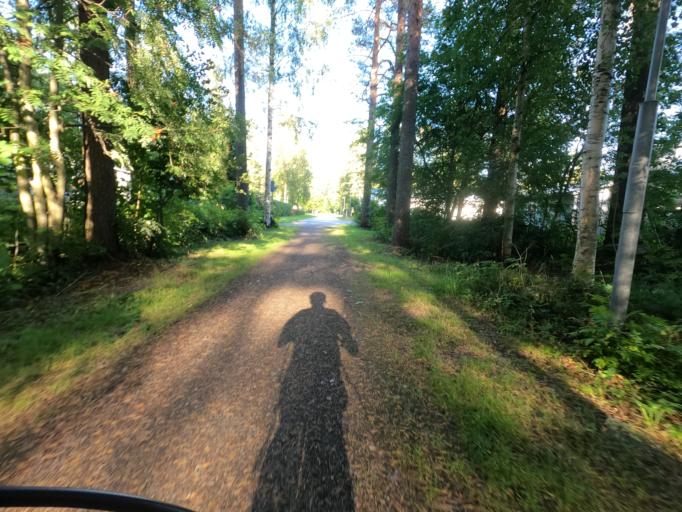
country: FI
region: North Karelia
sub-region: Joensuu
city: Joensuu
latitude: 62.6140
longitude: 29.7538
